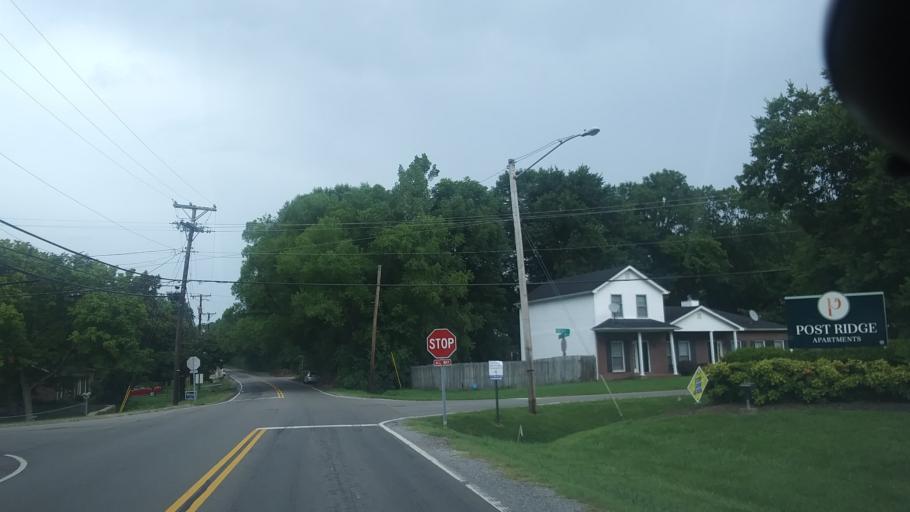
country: US
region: Tennessee
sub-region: Davidson County
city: Belle Meade
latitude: 36.0864
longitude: -86.9371
